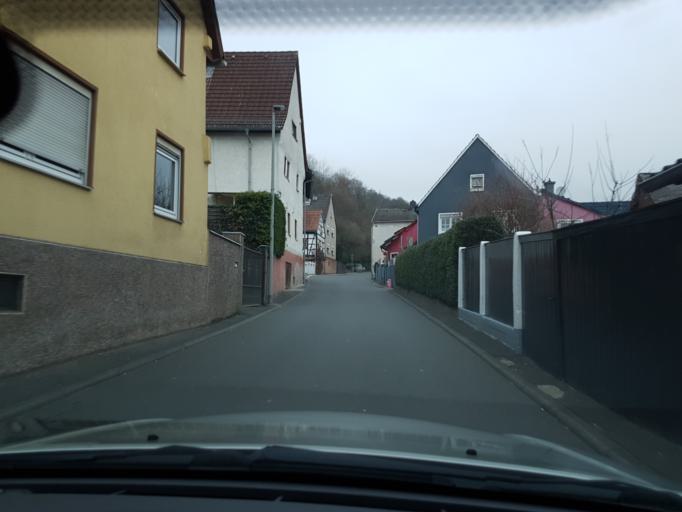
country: DE
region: Hesse
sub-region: Regierungsbezirk Darmstadt
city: Kiedrich
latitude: 50.0442
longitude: 8.0796
